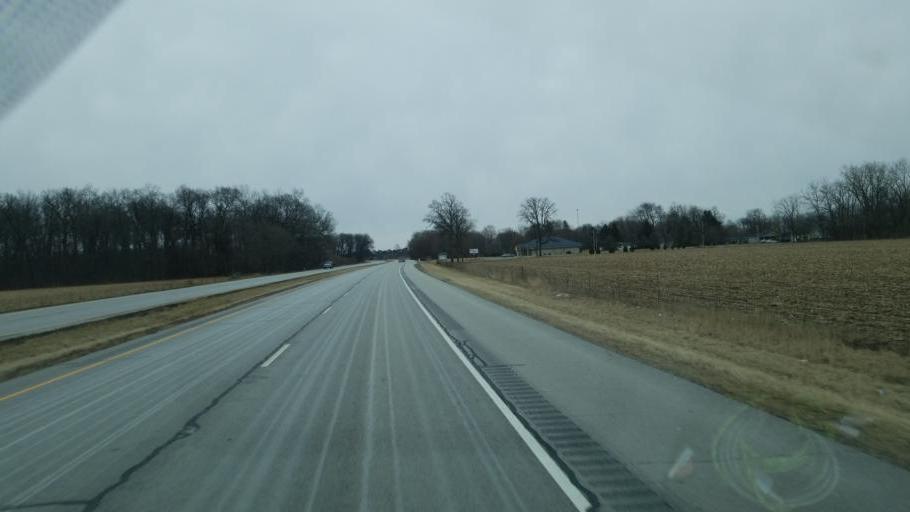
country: US
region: Indiana
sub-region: LaPorte County
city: Wanatah
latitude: 41.4357
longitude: -86.9274
